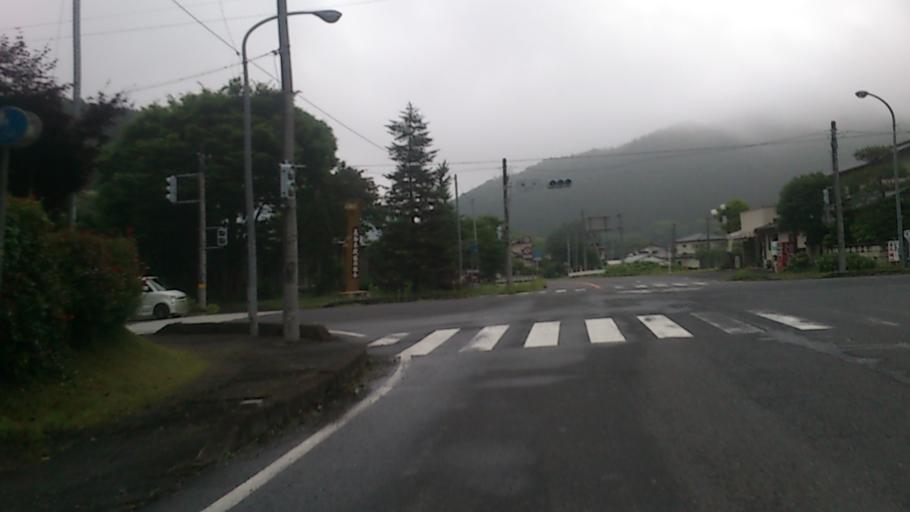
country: JP
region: Ibaraki
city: Daigo
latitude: 36.6569
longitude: 140.2860
